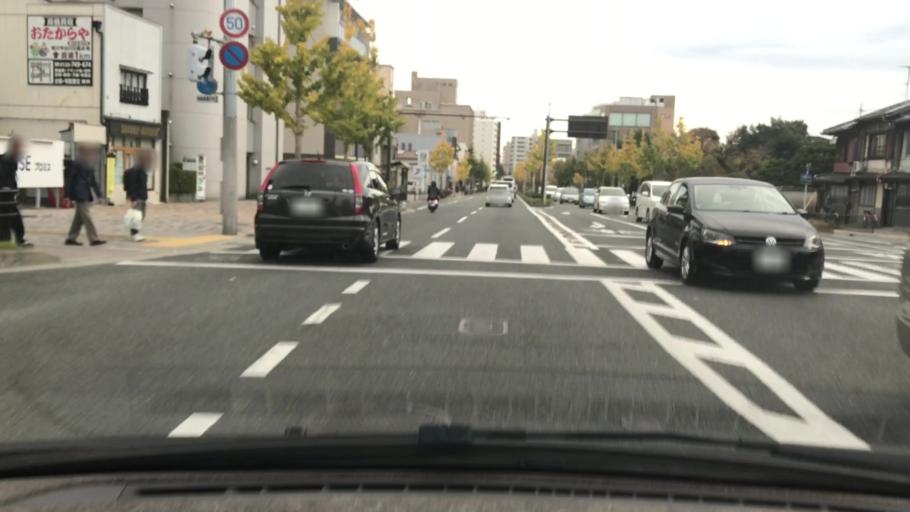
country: JP
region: Kyoto
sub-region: Kyoto-shi
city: Kamigyo-ku
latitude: 35.0406
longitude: 135.7518
